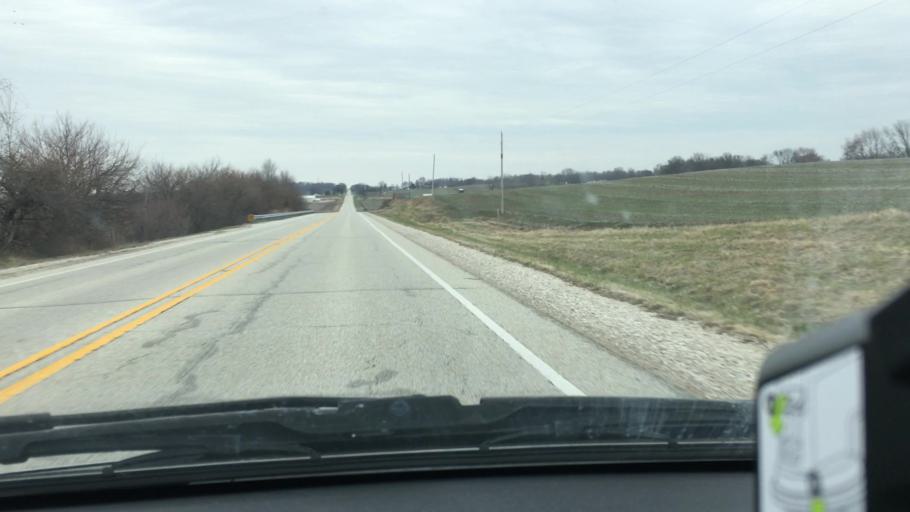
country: US
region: Indiana
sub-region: Greene County
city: Bloomfield
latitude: 38.9652
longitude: -87.0161
